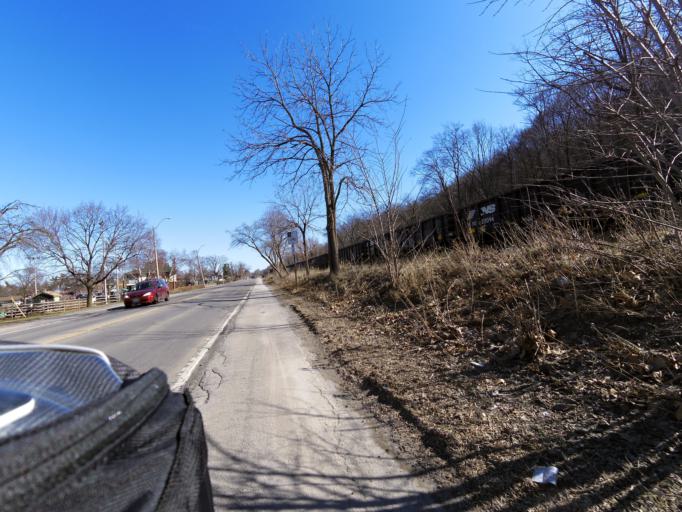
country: CA
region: Ontario
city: Hamilton
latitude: 43.2386
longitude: -79.8310
